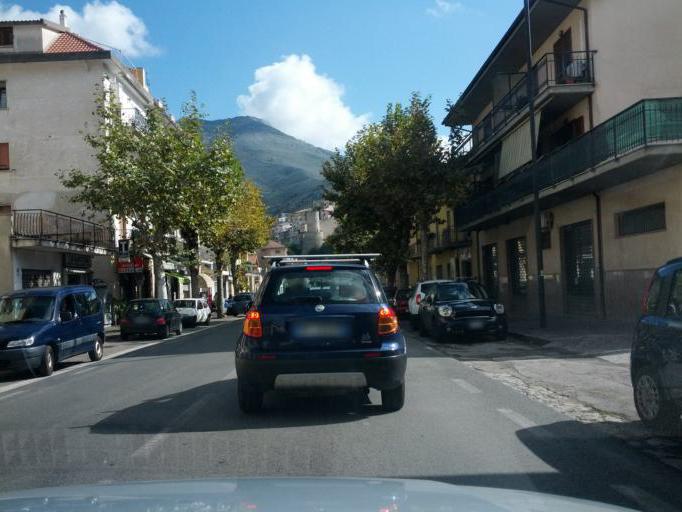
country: IT
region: Latium
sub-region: Provincia di Latina
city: Itri
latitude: 41.2898
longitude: 13.5253
